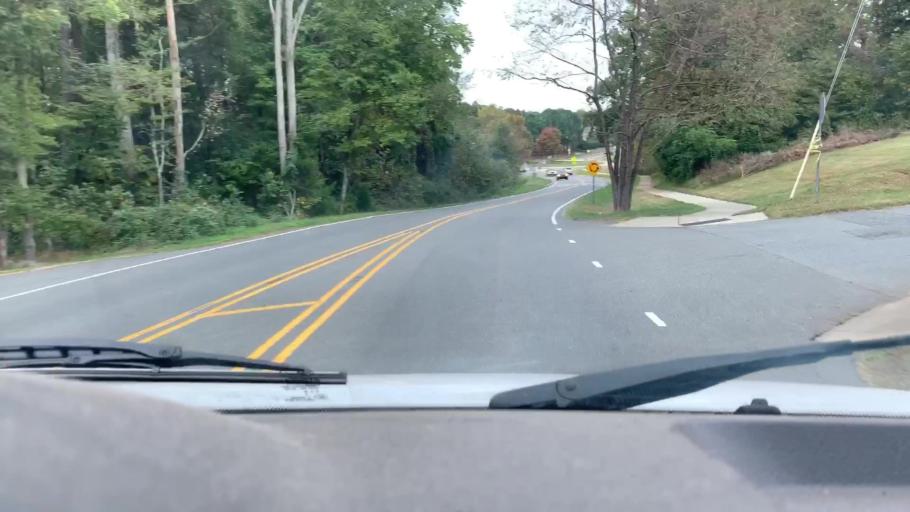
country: US
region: North Carolina
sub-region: Mecklenburg County
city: Huntersville
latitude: 35.4217
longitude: -80.8687
